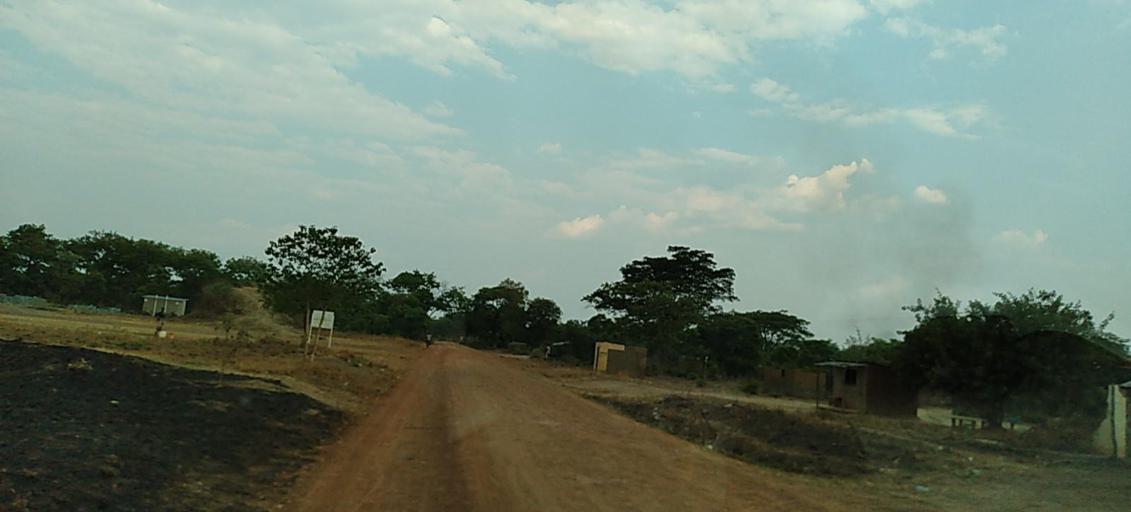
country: ZM
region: Copperbelt
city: Kalulushi
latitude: -13.0187
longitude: 27.9141
